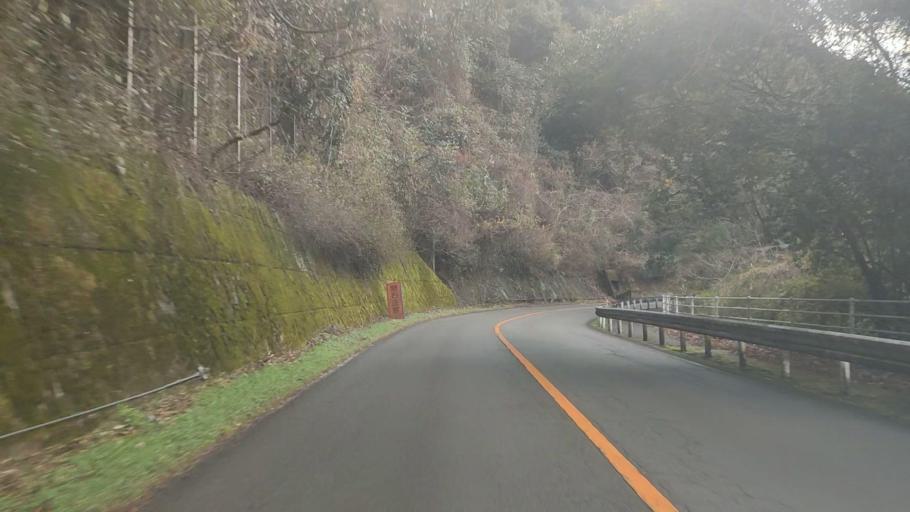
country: JP
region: Kumamoto
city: Hitoyoshi
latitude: 32.3003
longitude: 130.8465
